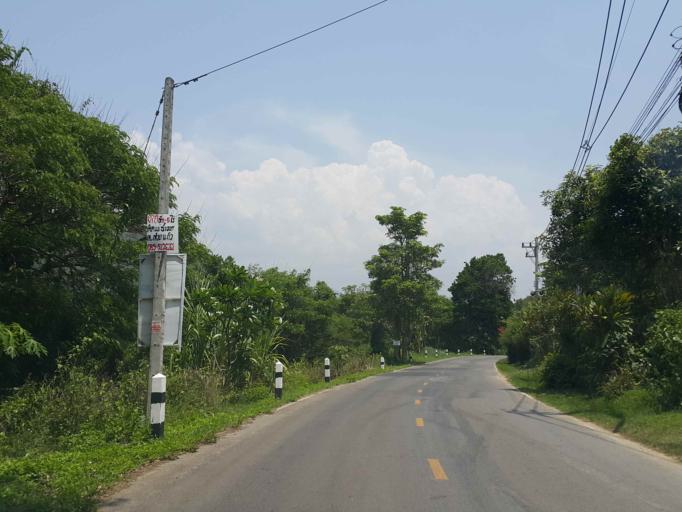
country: TH
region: Chiang Mai
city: Mae On
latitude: 18.9082
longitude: 99.2509
